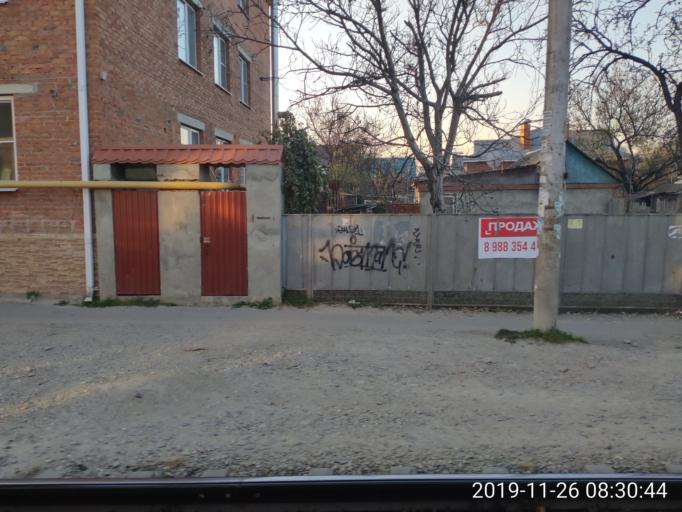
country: RU
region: Krasnodarskiy
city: Krasnodar
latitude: 45.0513
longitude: 39.0007
